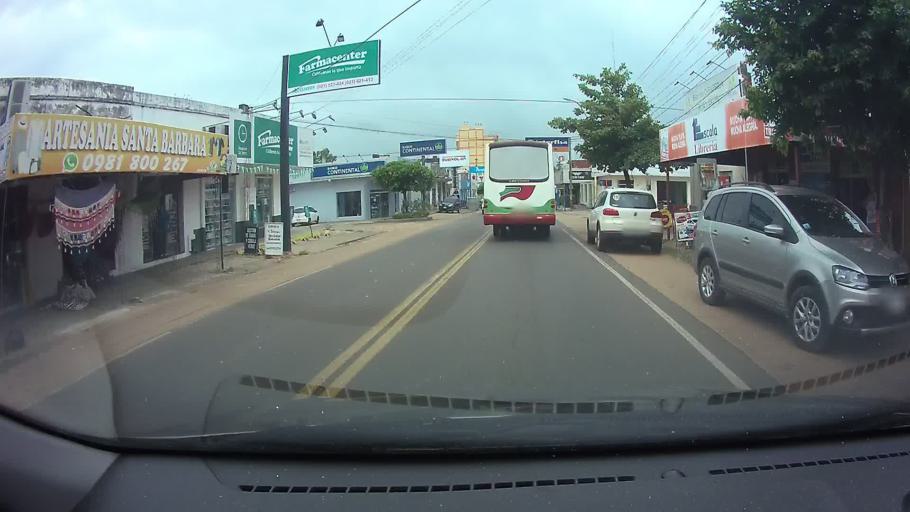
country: PY
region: Paraguari
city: Carapegua
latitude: -25.7679
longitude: -57.2403
